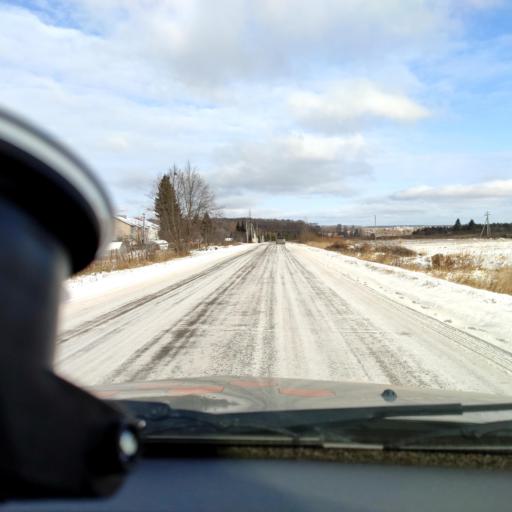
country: RU
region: Bashkortostan
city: Avdon
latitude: 54.7868
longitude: 55.7607
